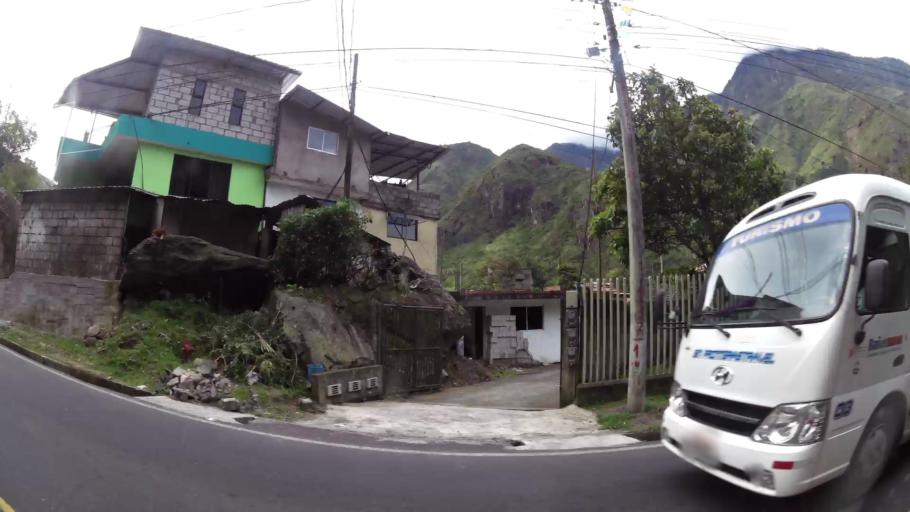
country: EC
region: Tungurahua
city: Banos
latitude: -1.3994
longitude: -78.3832
